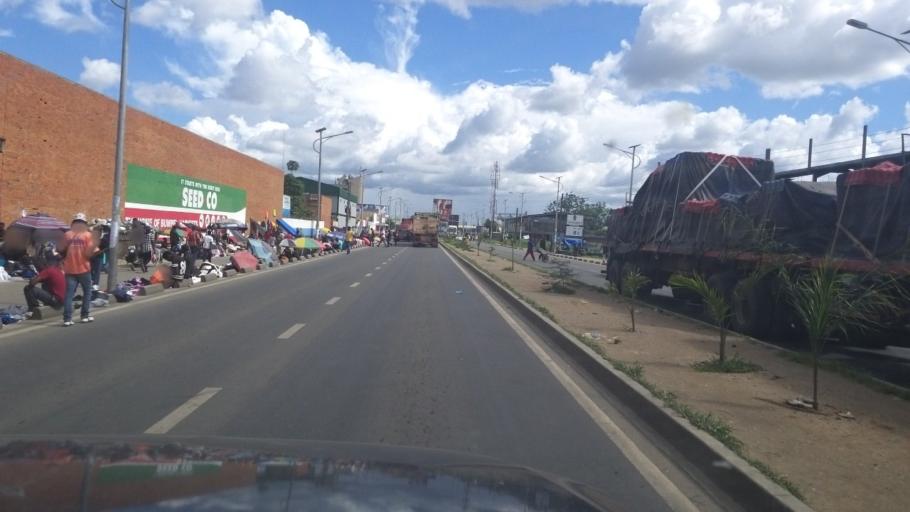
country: ZM
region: Lusaka
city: Lusaka
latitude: -15.4230
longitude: 28.2786
